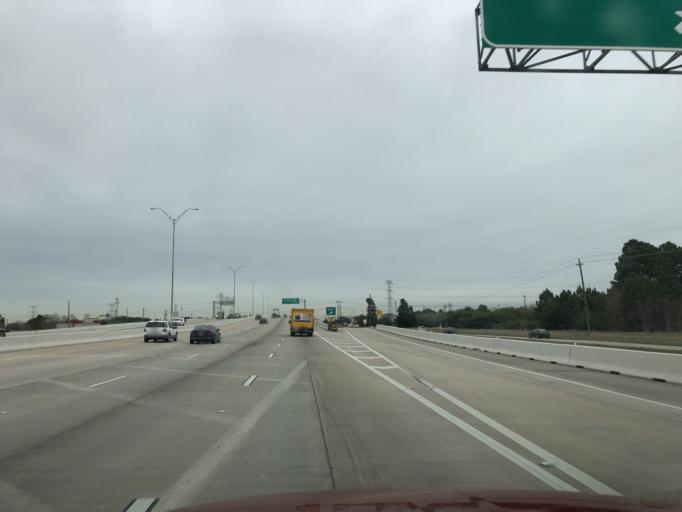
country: US
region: Texas
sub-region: Fort Bend County
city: Missouri City
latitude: 29.6190
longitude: -95.5040
